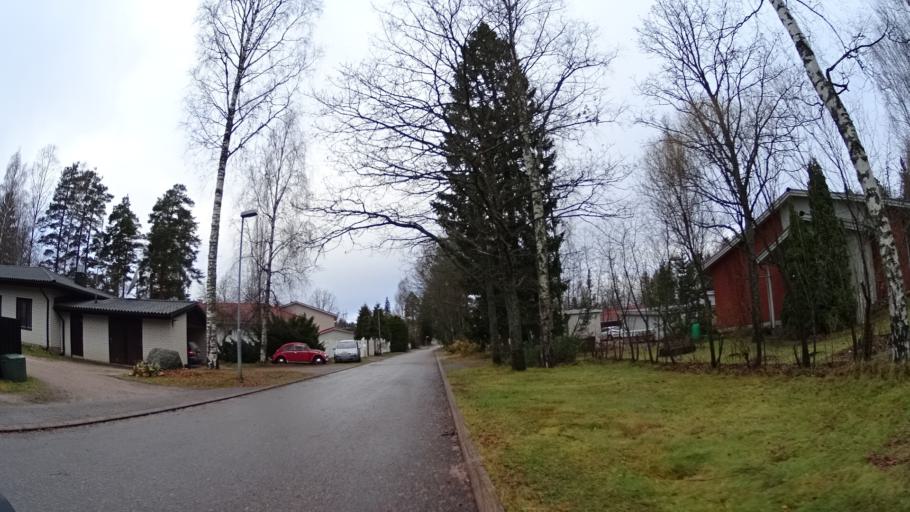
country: FI
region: Uusimaa
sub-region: Helsinki
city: Kauniainen
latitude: 60.2364
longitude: 24.6989
